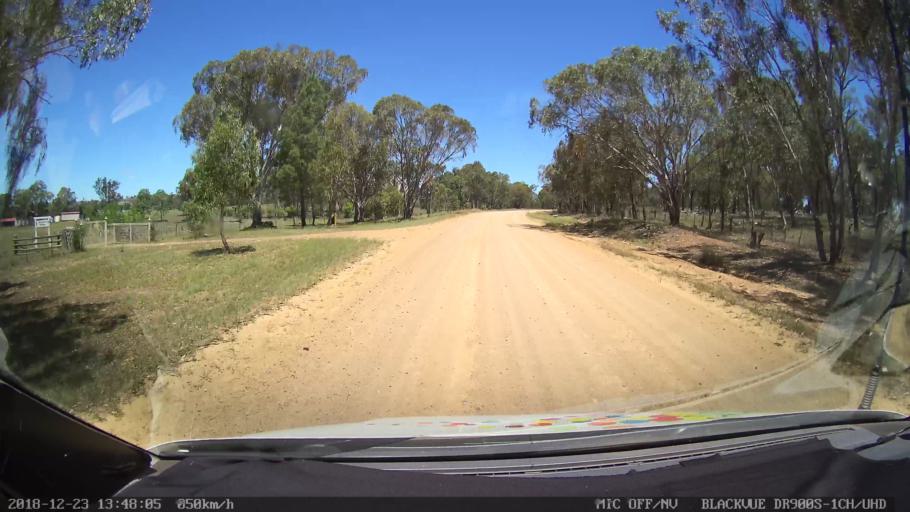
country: AU
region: New South Wales
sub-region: Tamworth Municipality
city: Manilla
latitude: -30.5147
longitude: 151.1160
